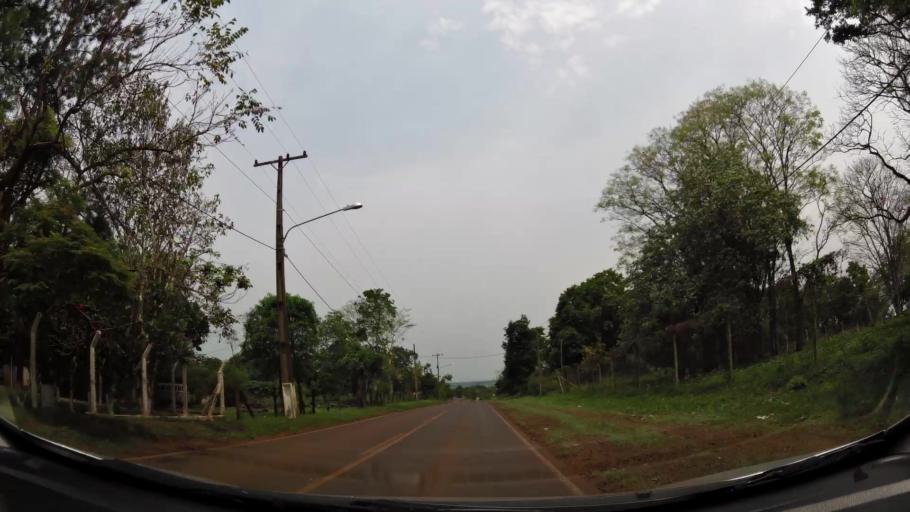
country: BR
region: Parana
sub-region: Foz Do Iguacu
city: Foz do Iguacu
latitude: -25.5793
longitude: -54.6030
